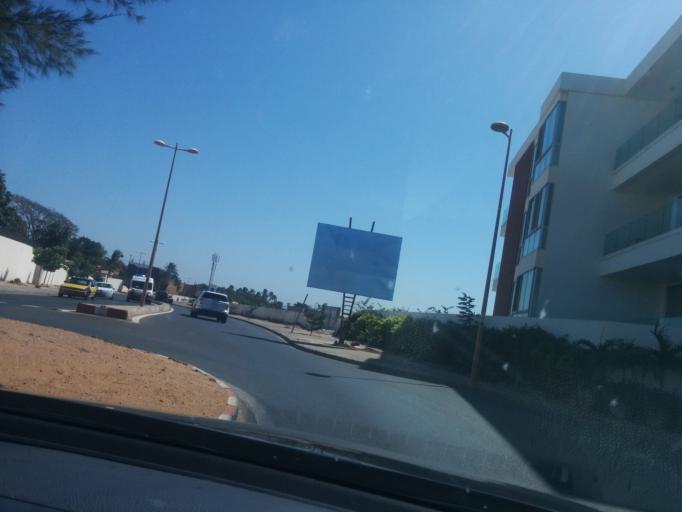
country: SN
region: Dakar
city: Mermoz Boabab
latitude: 14.7053
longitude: -17.4825
